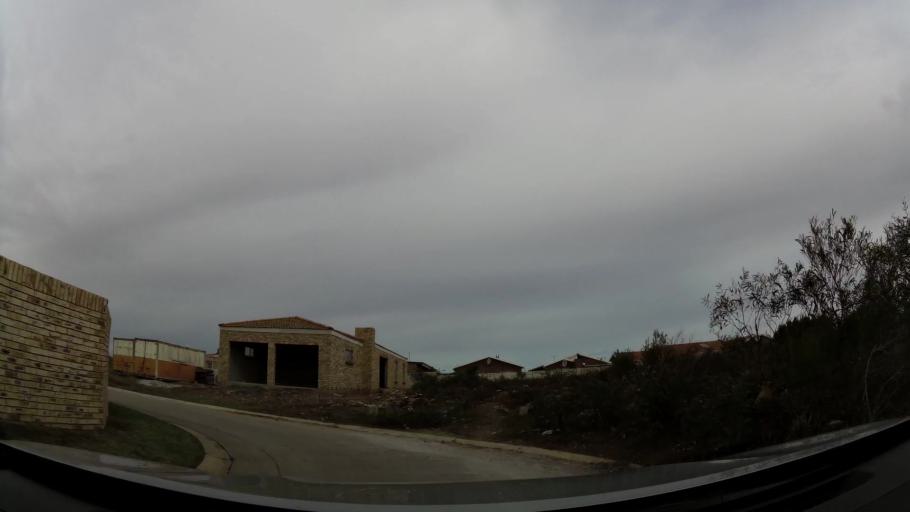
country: ZA
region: Eastern Cape
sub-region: Nelson Mandela Bay Metropolitan Municipality
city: Port Elizabeth
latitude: -33.9311
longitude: 25.5026
